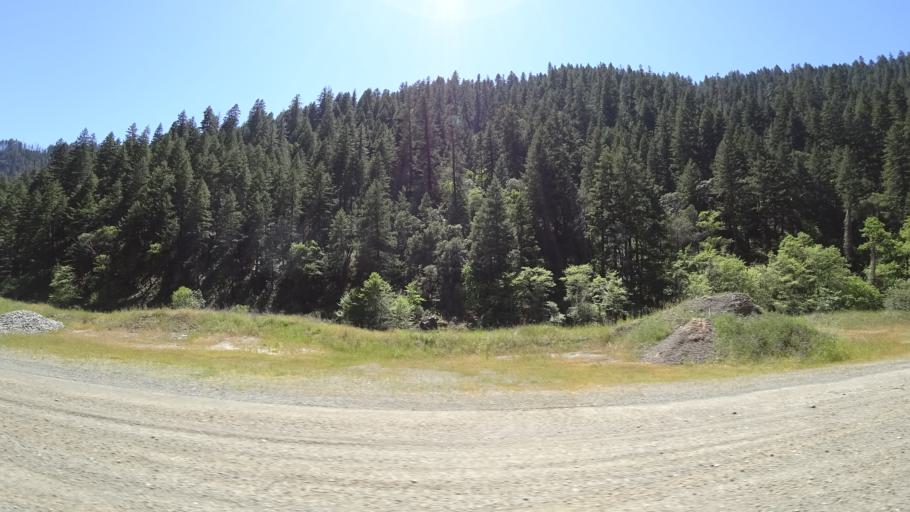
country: US
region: California
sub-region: Trinity County
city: Hayfork
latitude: 40.7723
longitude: -123.3104
